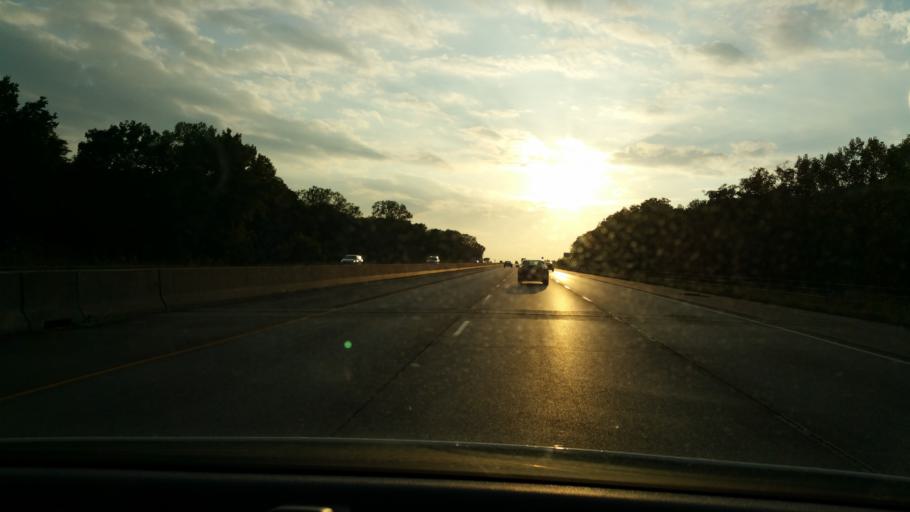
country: US
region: Iowa
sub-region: Polk County
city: Urbandale
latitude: 41.6527
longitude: -93.7171
